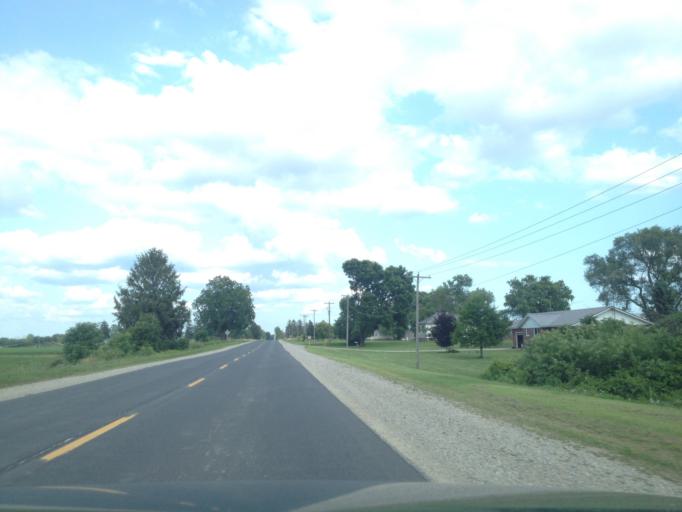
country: CA
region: Ontario
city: Aylmer
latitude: 42.6746
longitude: -80.9251
